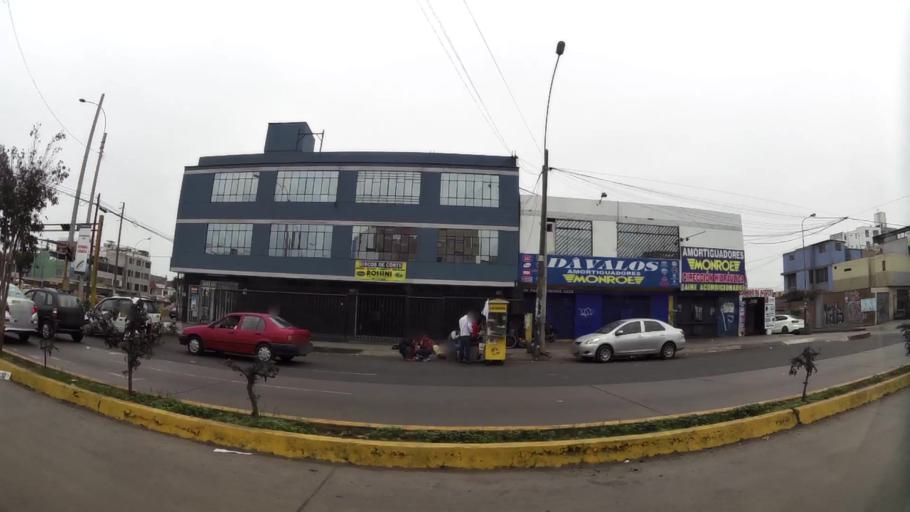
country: PE
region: Lima
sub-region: Lima
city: San Luis
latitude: -12.0809
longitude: -77.0192
